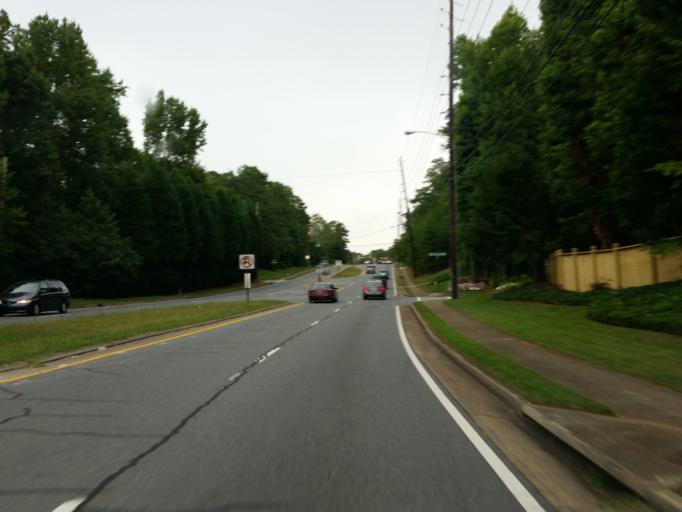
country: US
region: Georgia
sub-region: Fulton County
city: Roswell
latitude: 34.0578
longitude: -84.4404
